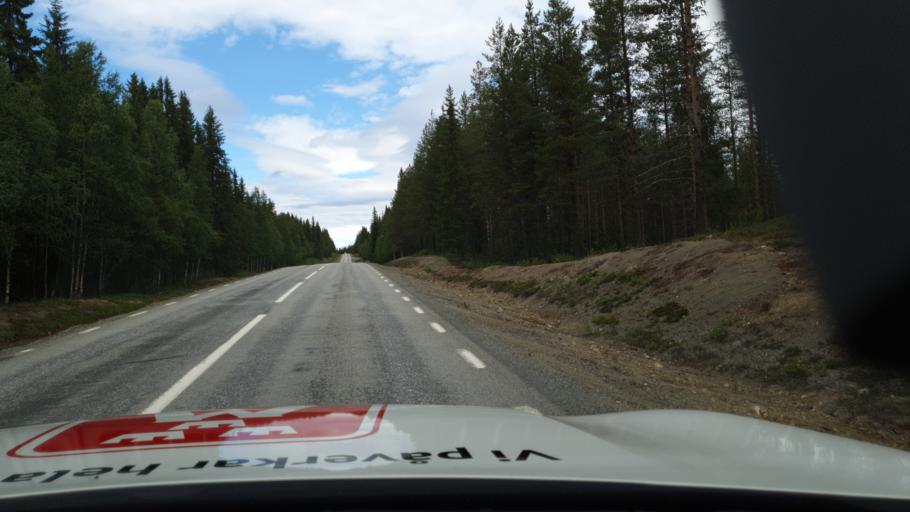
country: SE
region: Vaesterbotten
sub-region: Storumans Kommun
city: Fristad
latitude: 65.3445
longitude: 16.6030
